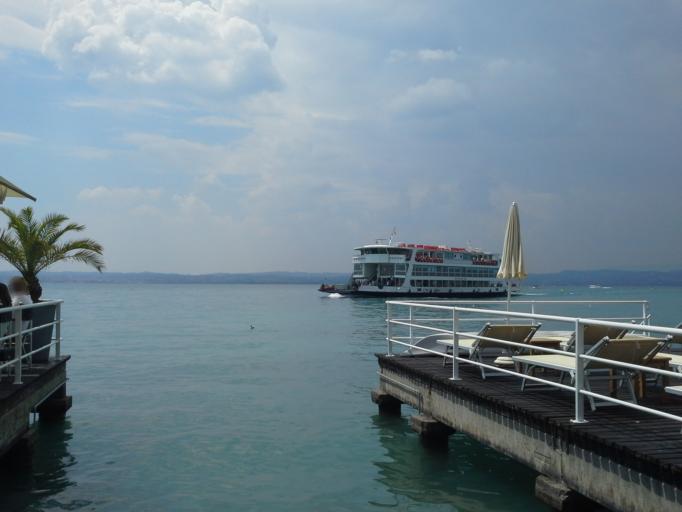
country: IT
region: Lombardy
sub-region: Provincia di Brescia
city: Sirmione
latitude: 45.4927
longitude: 10.6065
